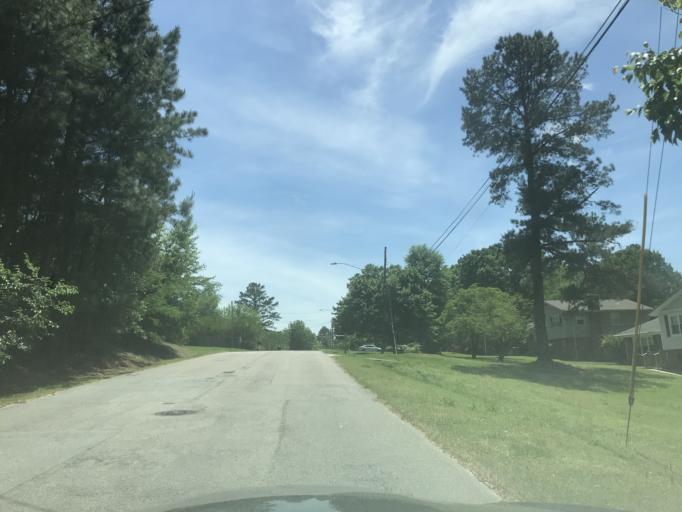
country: US
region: North Carolina
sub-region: Wake County
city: Raleigh
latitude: 35.8219
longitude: -78.5804
